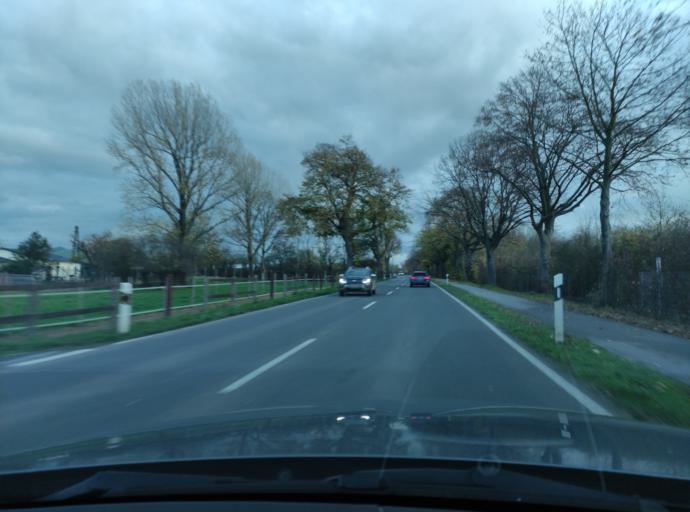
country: DE
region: North Rhine-Westphalia
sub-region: Regierungsbezirk Dusseldorf
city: Dormagen
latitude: 51.1055
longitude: 6.7888
